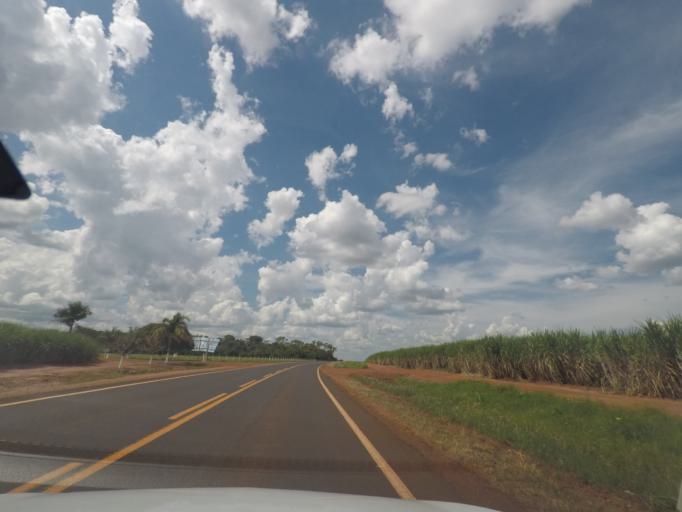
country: BR
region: Minas Gerais
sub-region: Conceicao Das Alagoas
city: Conceicao das Alagoas
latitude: -19.8509
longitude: -48.5980
